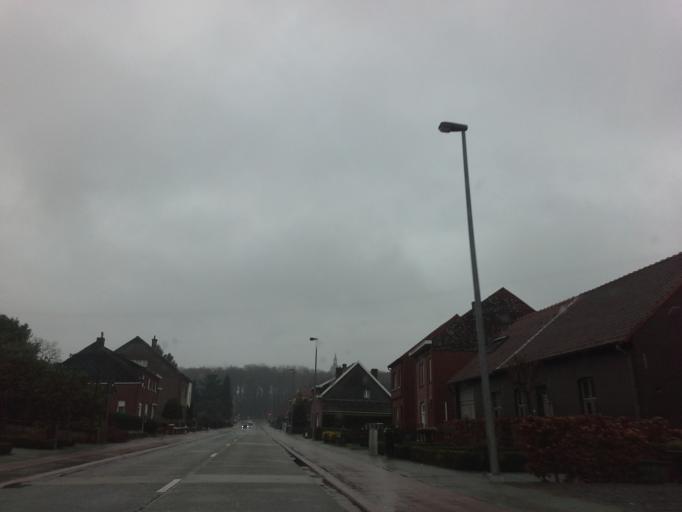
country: BE
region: Flanders
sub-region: Provincie Vlaams-Brabant
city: Scherpenheuvel-Zichem
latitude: 51.0277
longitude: 4.9757
